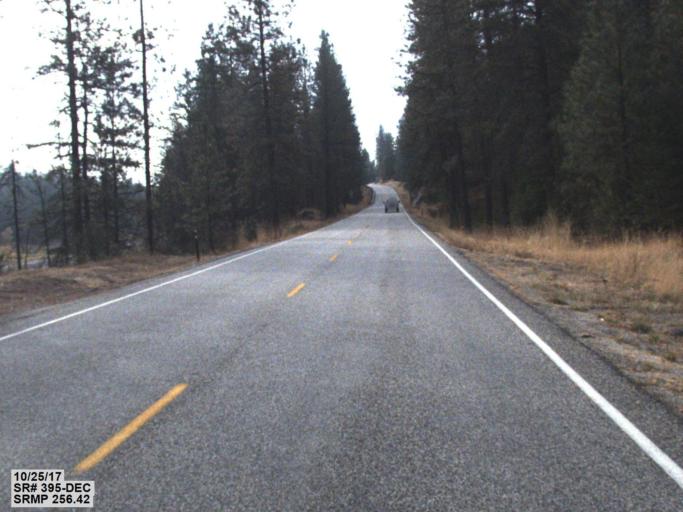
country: US
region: Washington
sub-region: Stevens County
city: Kettle Falls
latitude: 48.8213
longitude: -118.1701
